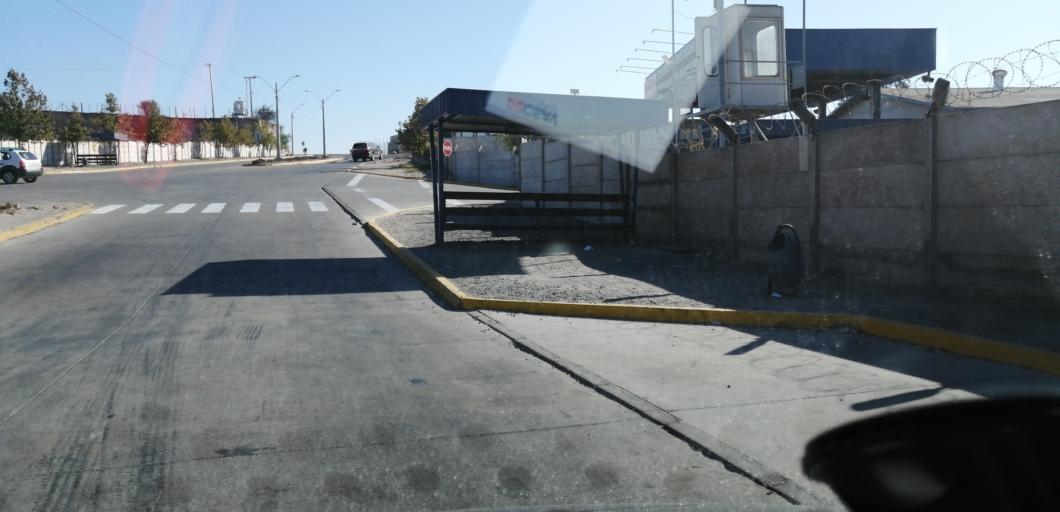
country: CL
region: Santiago Metropolitan
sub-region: Provincia de Santiago
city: Lo Prado
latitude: -33.4544
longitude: -70.7981
